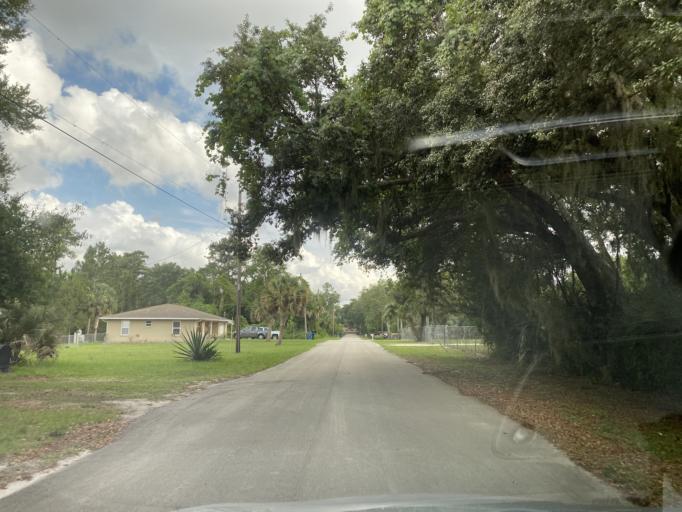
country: US
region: Florida
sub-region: Volusia County
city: Deltona
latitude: 28.8728
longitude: -81.2637
